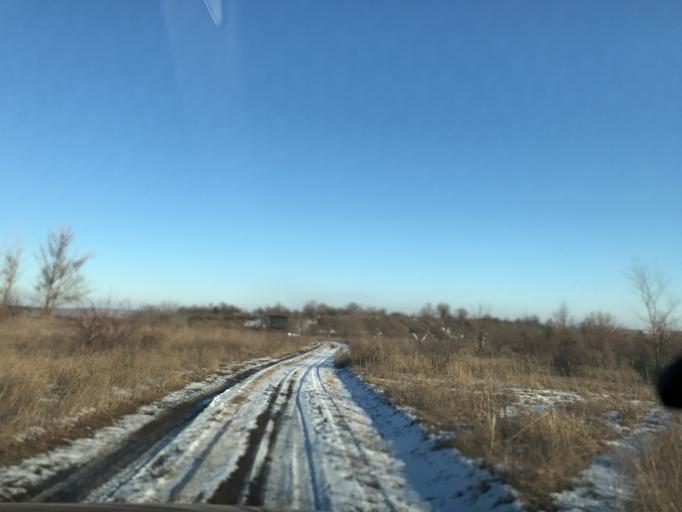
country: RU
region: Rostov
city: Staraya Stanitsa
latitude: 48.2409
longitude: 40.3959
